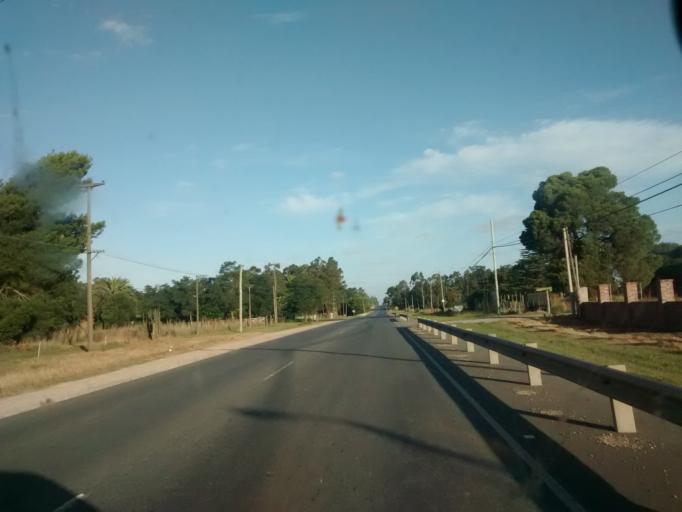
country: AR
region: Buenos Aires
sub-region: Partido de Loberia
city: Loberia
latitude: -38.1898
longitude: -58.7485
